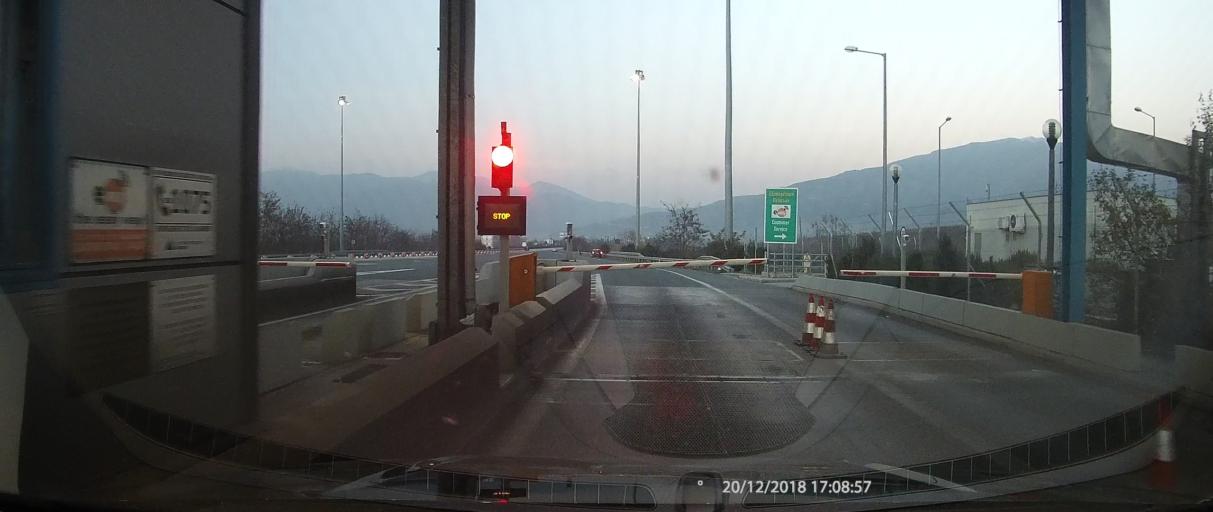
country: GR
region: Thessaly
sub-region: Nomos Larisis
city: Makrychori
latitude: 39.8043
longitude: 22.5029
